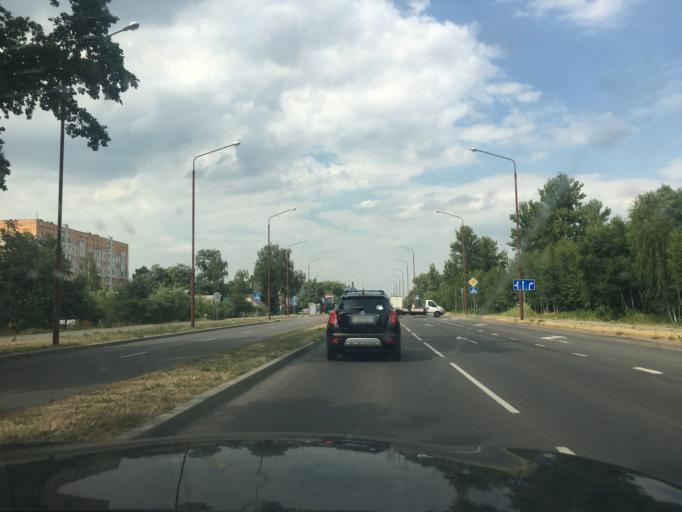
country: BY
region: Brest
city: Brest
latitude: 52.1339
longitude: 23.6751
